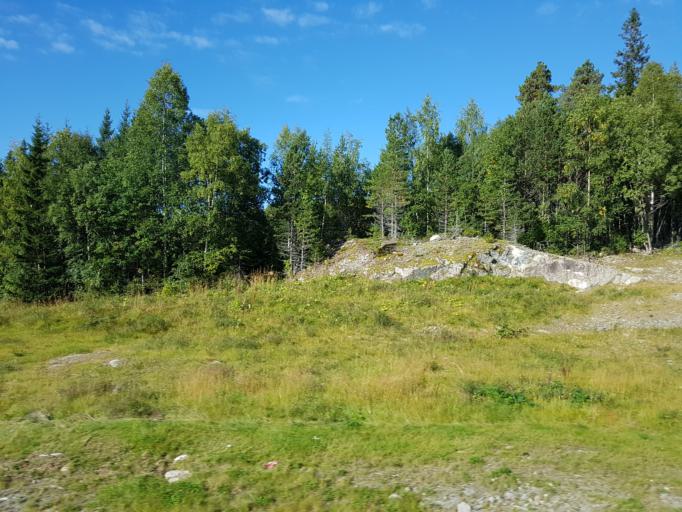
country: NO
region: Sor-Trondelag
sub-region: Trondheim
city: Trondheim
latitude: 63.6093
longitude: 10.2378
